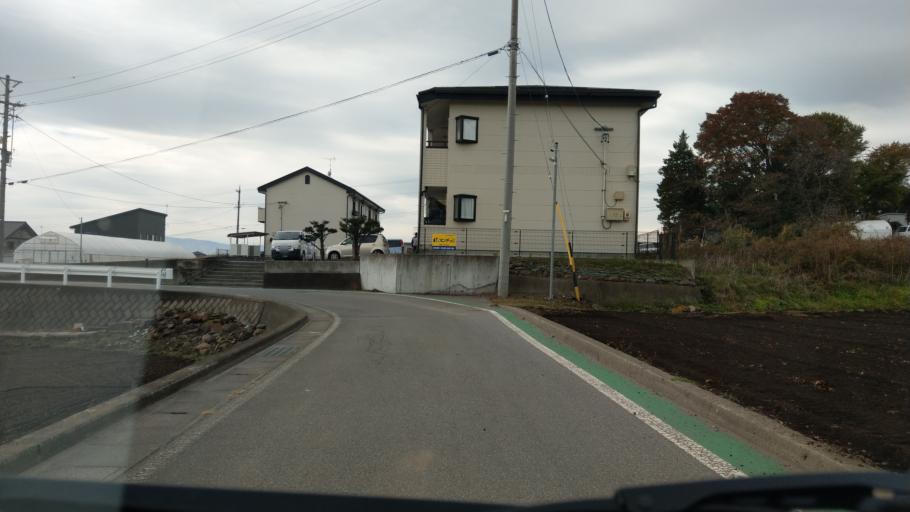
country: JP
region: Nagano
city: Komoro
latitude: 36.3196
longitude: 138.4602
